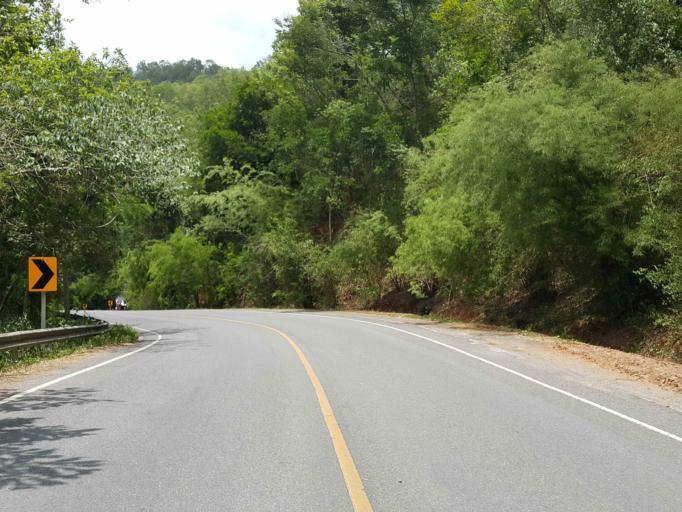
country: TH
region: Chiang Mai
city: Hang Dong
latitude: 18.7560
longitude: 98.8808
